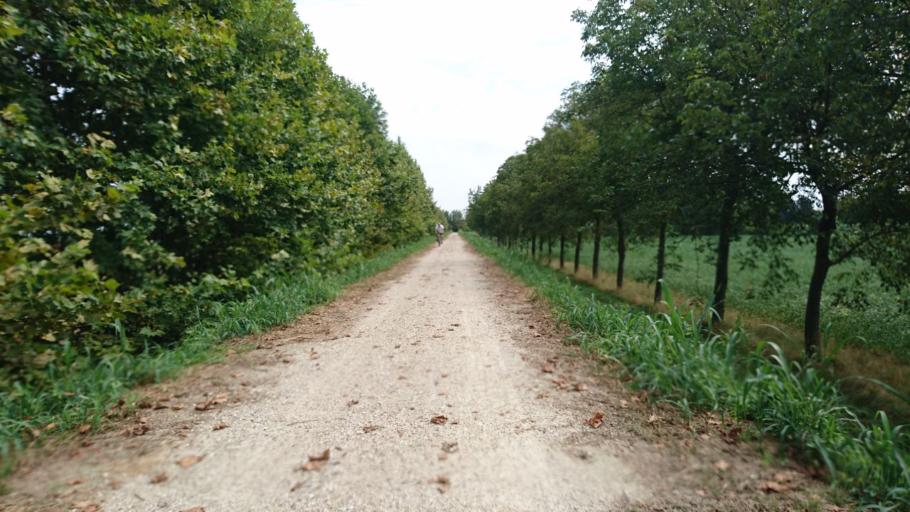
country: IT
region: Veneto
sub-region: Provincia di Vicenza
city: Longare
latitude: 45.4763
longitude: 11.6204
